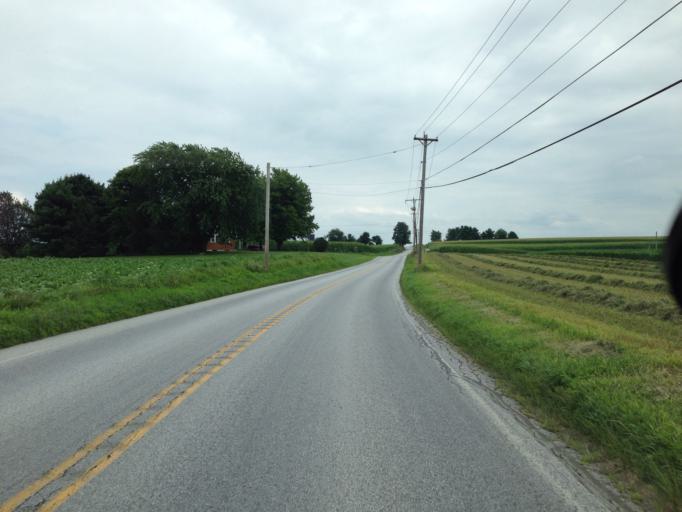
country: US
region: Pennsylvania
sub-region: Chester County
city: Oxford
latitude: 39.8513
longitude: -75.9613
